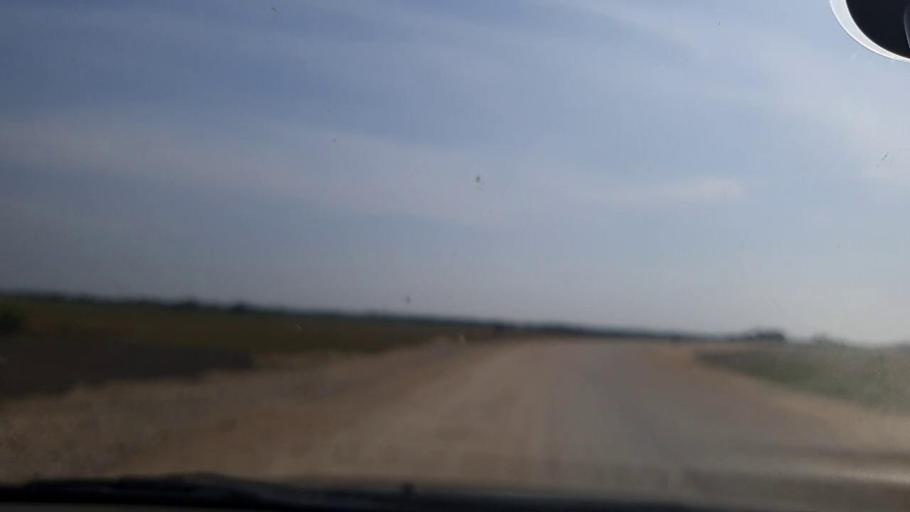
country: PK
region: Sindh
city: Mirpur Batoro
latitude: 24.7316
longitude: 68.2762
